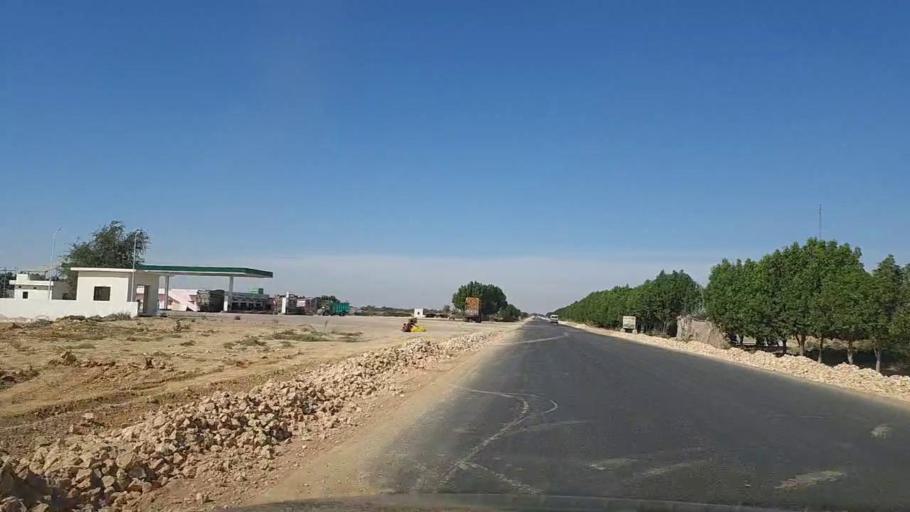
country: PK
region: Sindh
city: Kotri
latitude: 25.2675
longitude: 68.2189
